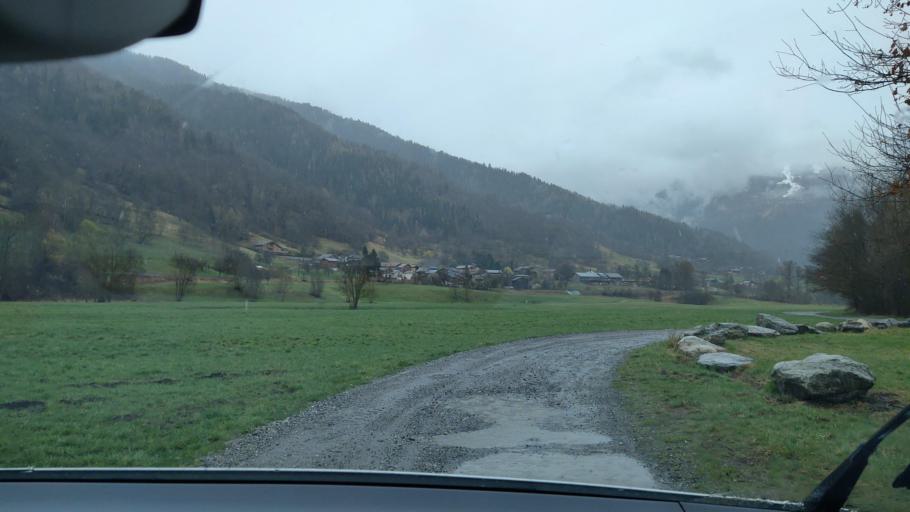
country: FR
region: Rhone-Alpes
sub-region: Departement de la Savoie
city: Bourg-Saint-Maurice
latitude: 45.5894
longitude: 6.7510
